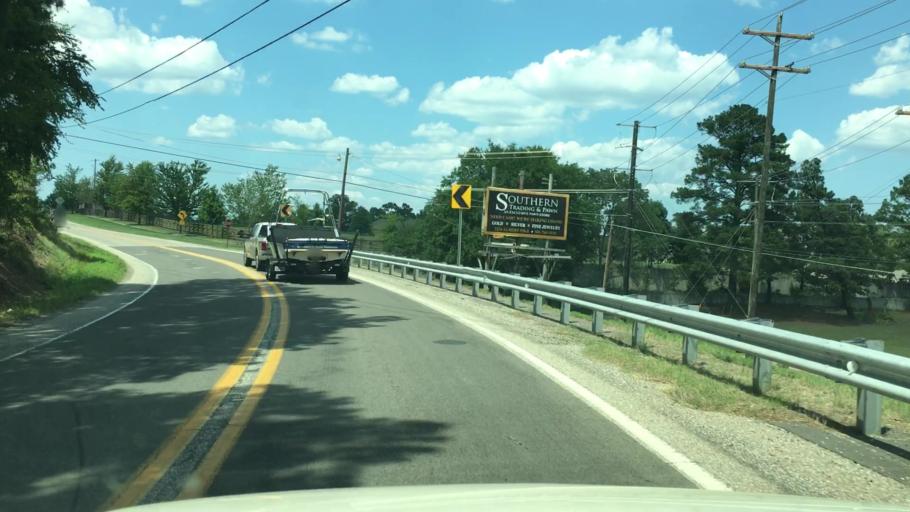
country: US
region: Arkansas
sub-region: Garland County
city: Lake Hamilton
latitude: 34.4053
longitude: -93.0907
